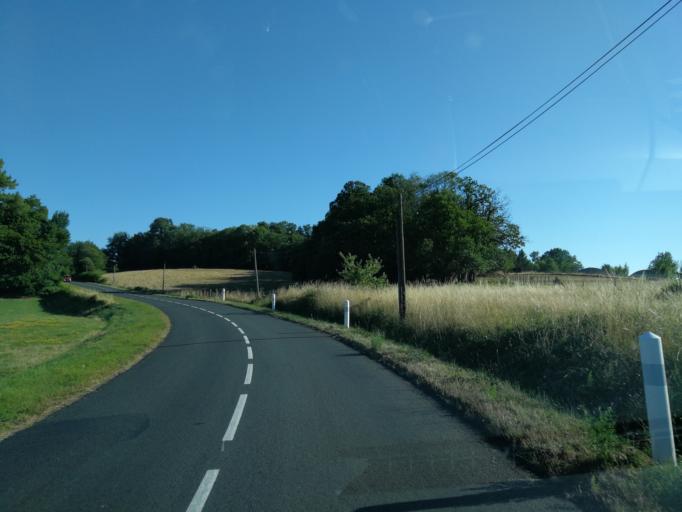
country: FR
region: Midi-Pyrenees
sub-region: Departement du Lot
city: Salviac
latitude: 44.6113
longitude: 1.2012
